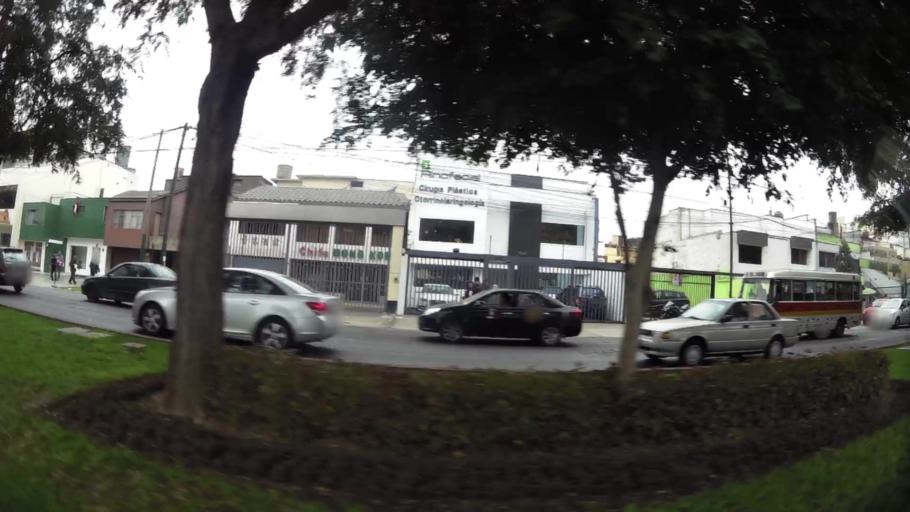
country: PE
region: Lima
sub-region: Lima
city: Surco
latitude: -12.1285
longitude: -76.9955
